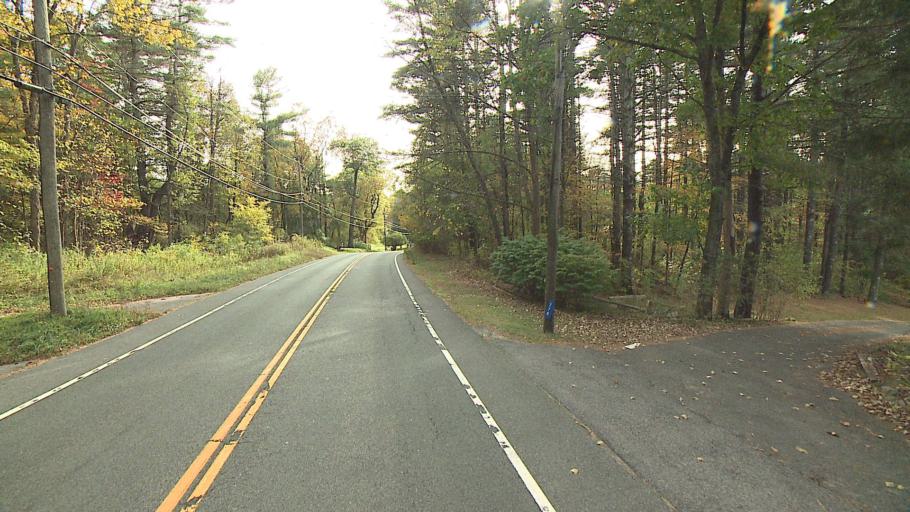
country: US
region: Connecticut
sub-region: Litchfield County
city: Canaan
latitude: 42.0203
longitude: -73.3482
